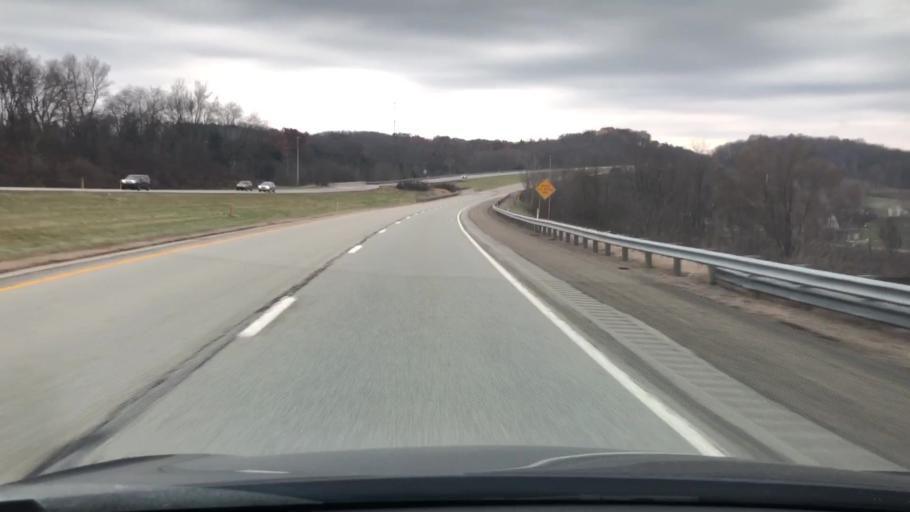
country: US
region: Pennsylvania
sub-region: Armstrong County
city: Freeport
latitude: 40.7267
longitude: -79.6682
